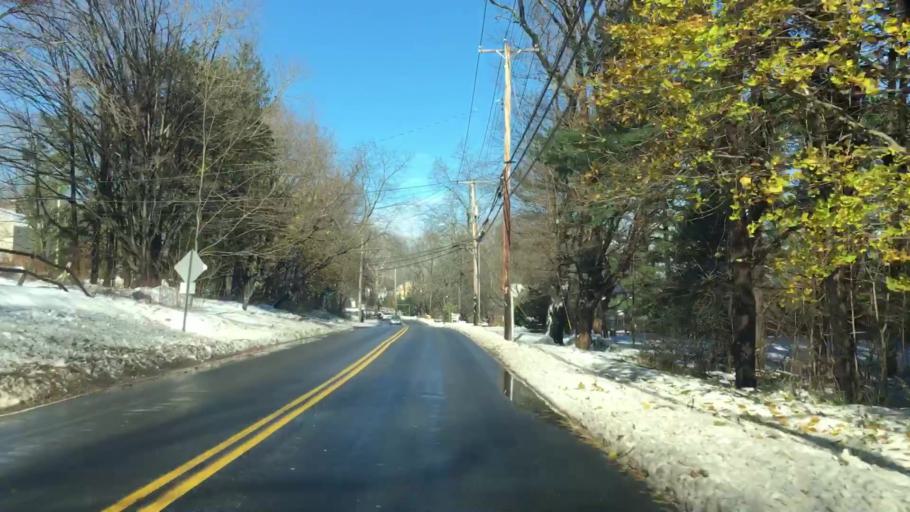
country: US
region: Connecticut
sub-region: Fairfield County
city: Shelton
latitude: 41.2870
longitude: -73.1401
